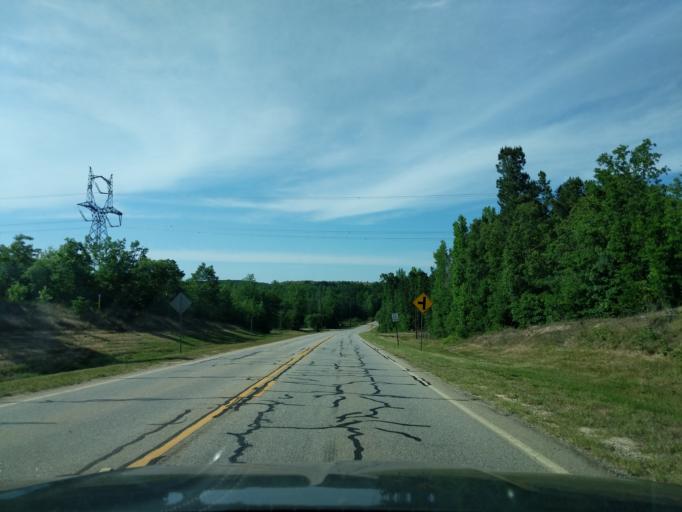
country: US
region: Georgia
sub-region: Jefferson County
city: Wrens
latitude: 33.2700
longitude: -82.3862
